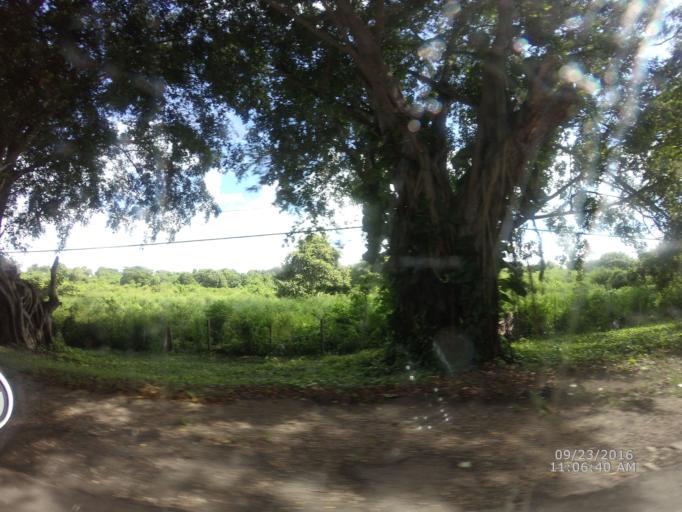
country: CU
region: Mayabeque
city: Jamaica
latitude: 23.0121
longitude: -82.2238
